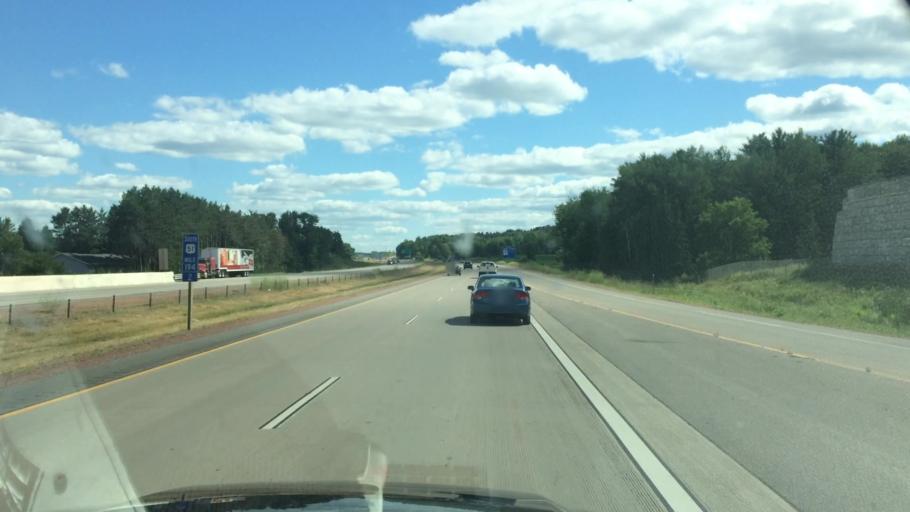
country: US
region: Wisconsin
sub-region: Marathon County
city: Wausau
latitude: 44.9838
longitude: -89.6572
